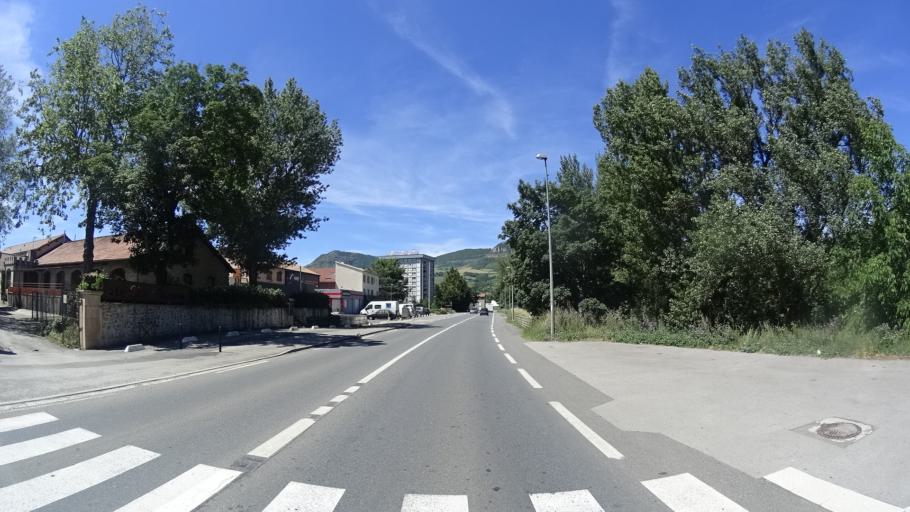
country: FR
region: Midi-Pyrenees
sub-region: Departement de l'Aveyron
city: Millau
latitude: 44.1034
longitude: 3.0849
